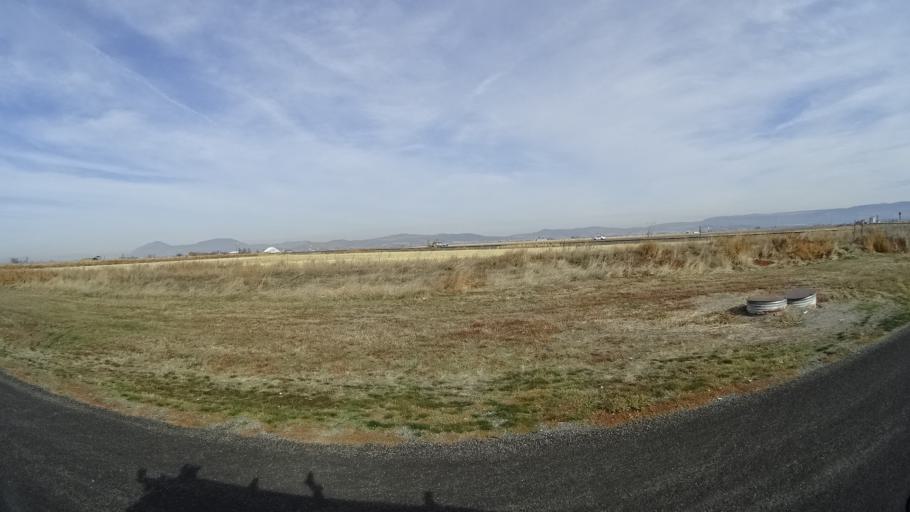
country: US
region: California
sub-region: Siskiyou County
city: Tulelake
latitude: 41.9607
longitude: -121.4796
